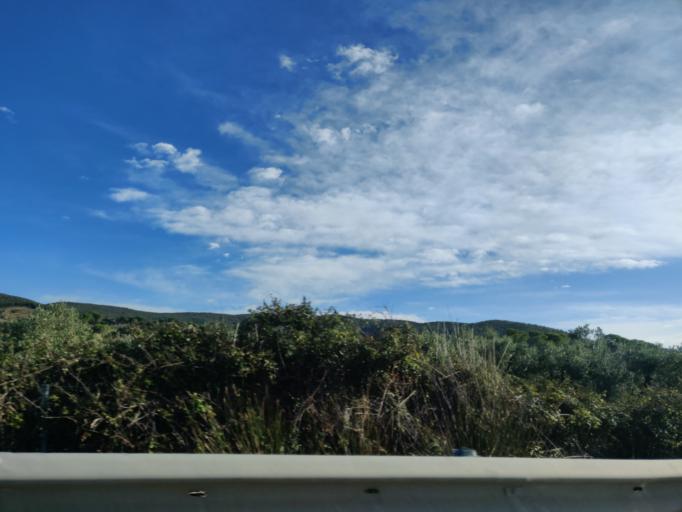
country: IT
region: Tuscany
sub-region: Provincia di Grosseto
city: Gavorrano
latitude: 42.9514
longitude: 10.8791
